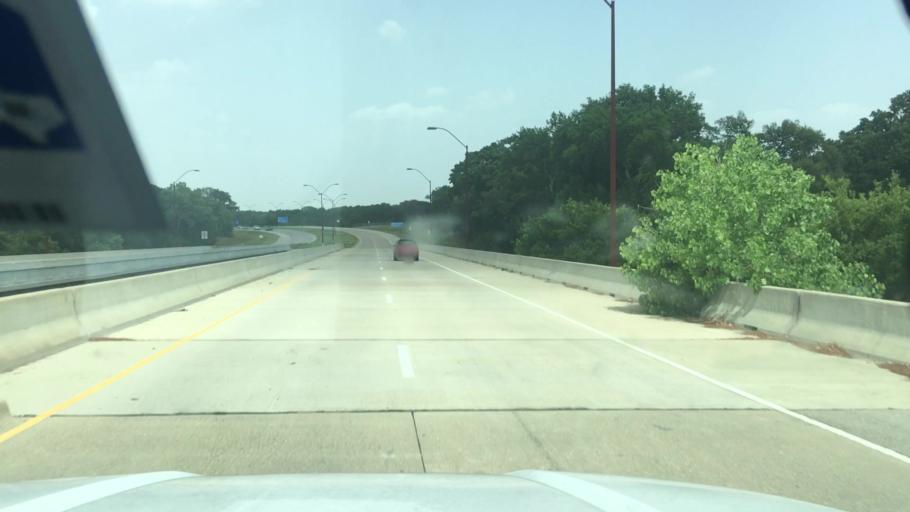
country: US
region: Texas
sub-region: Tarrant County
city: Euless
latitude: 32.8671
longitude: -97.0612
